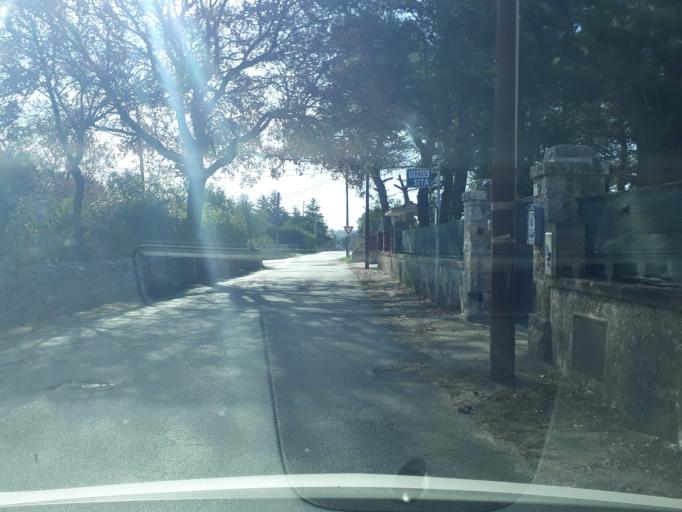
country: IT
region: Apulia
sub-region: Provincia di Brindisi
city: Lamie di Olimpie-Selva
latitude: 40.7938
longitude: 17.3546
